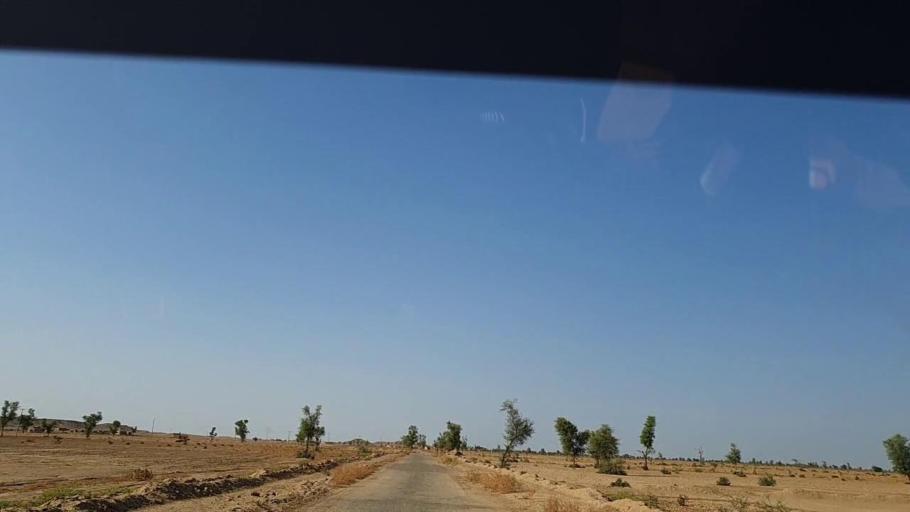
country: PK
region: Sindh
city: Johi
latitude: 26.5334
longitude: 67.5077
